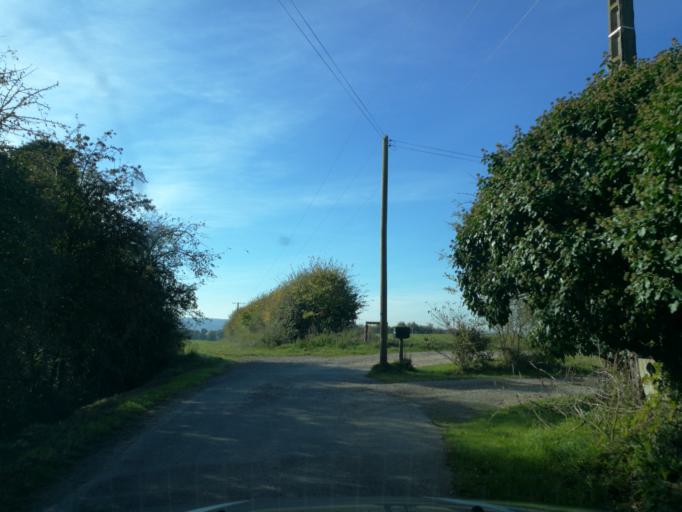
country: FR
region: Brittany
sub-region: Departement d'Ille-et-Vilaine
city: Montfort-sur-Meu
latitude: 48.1563
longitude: -1.9513
